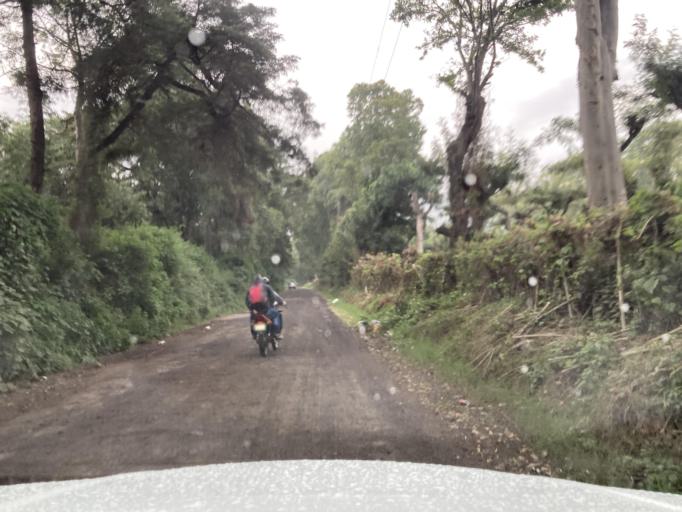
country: GT
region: Sacatepequez
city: San Miguel Duenas
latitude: 14.5233
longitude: -90.8110
